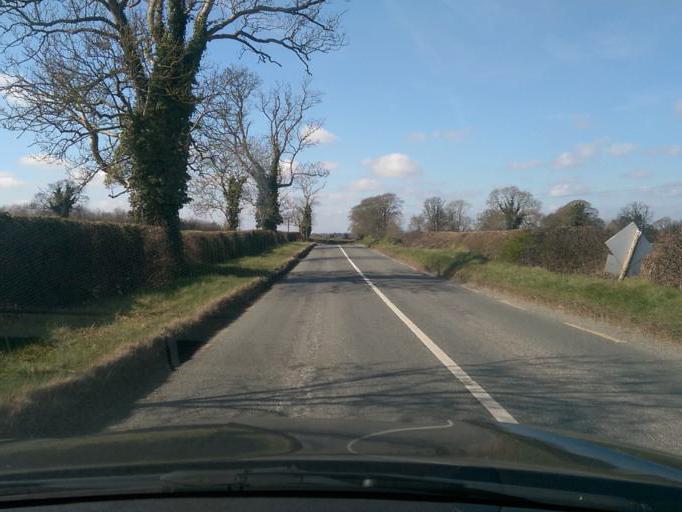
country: IE
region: Leinster
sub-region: Kildare
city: Maynooth
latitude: 53.3671
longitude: -6.5682
